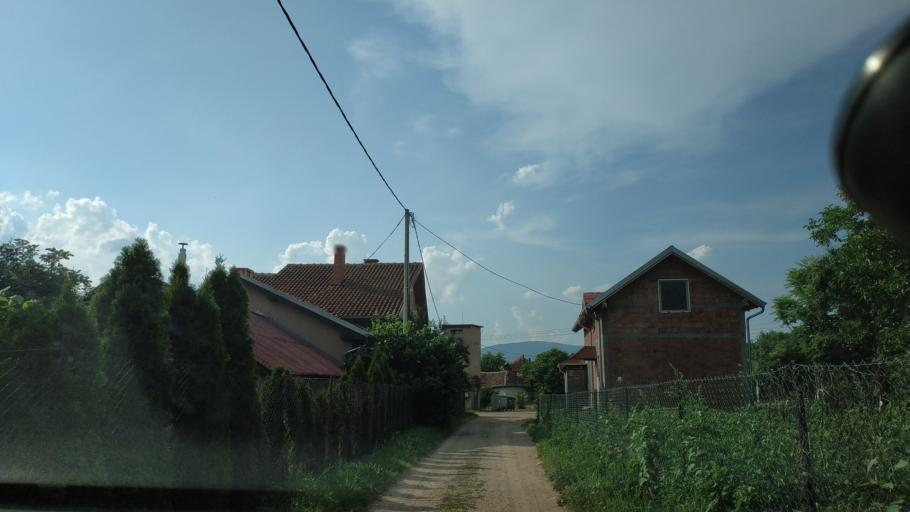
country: RS
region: Central Serbia
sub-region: Nisavski Okrug
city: Aleksinac
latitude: 43.6031
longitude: 21.6906
